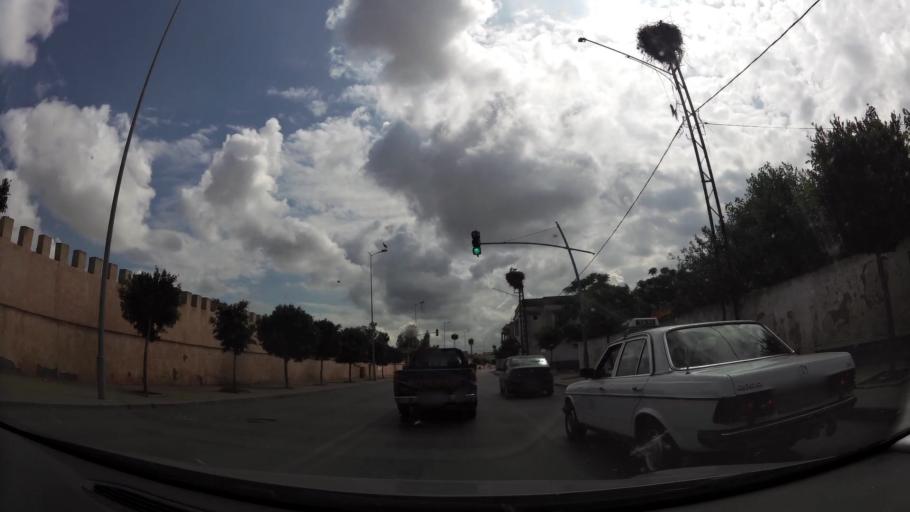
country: MA
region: Gharb-Chrarda-Beni Hssen
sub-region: Kenitra Province
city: Kenitra
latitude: 34.2664
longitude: -6.5760
